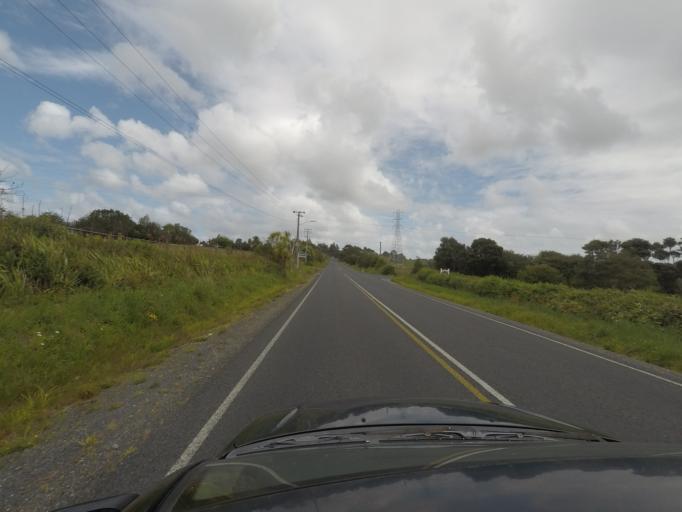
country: NZ
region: Auckland
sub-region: Auckland
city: Parakai
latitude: -36.6312
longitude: 174.5035
